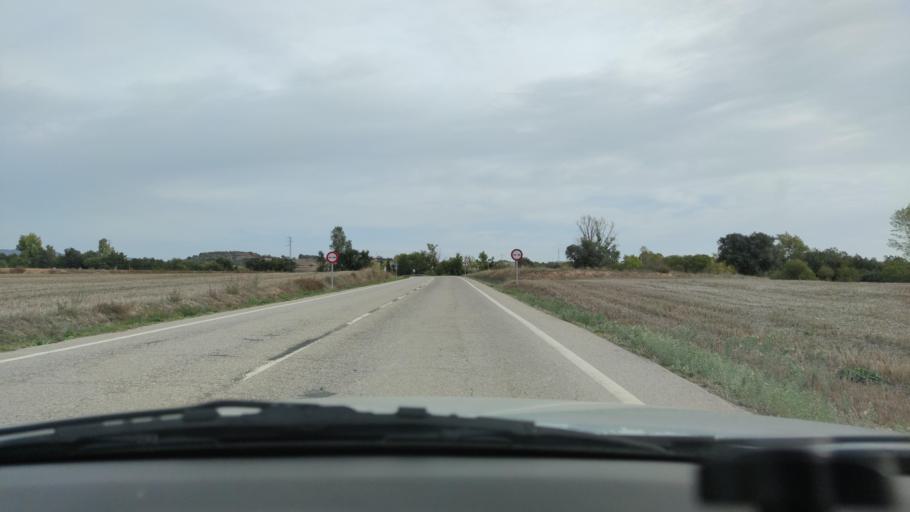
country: ES
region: Catalonia
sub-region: Provincia de Lleida
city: Artesa de Segre
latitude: 41.9168
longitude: 1.0732
